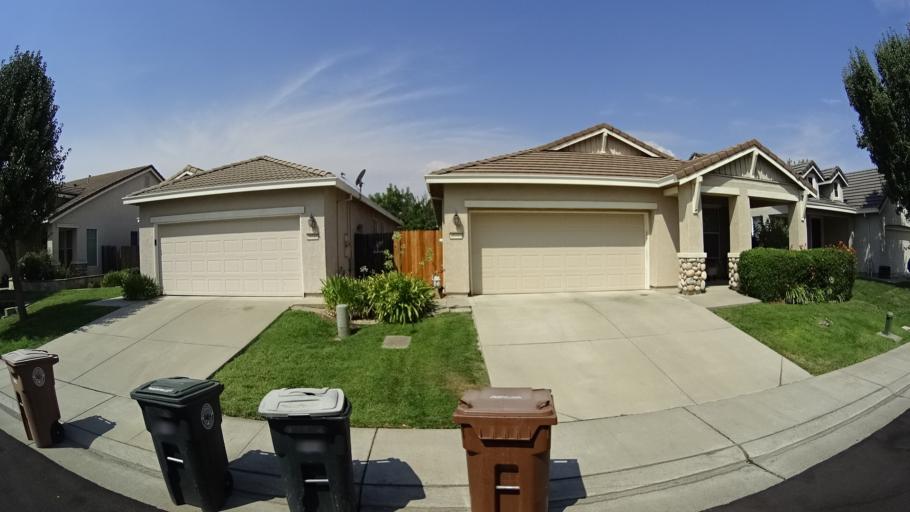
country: US
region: California
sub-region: Sacramento County
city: Laguna
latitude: 38.3921
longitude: -121.4471
